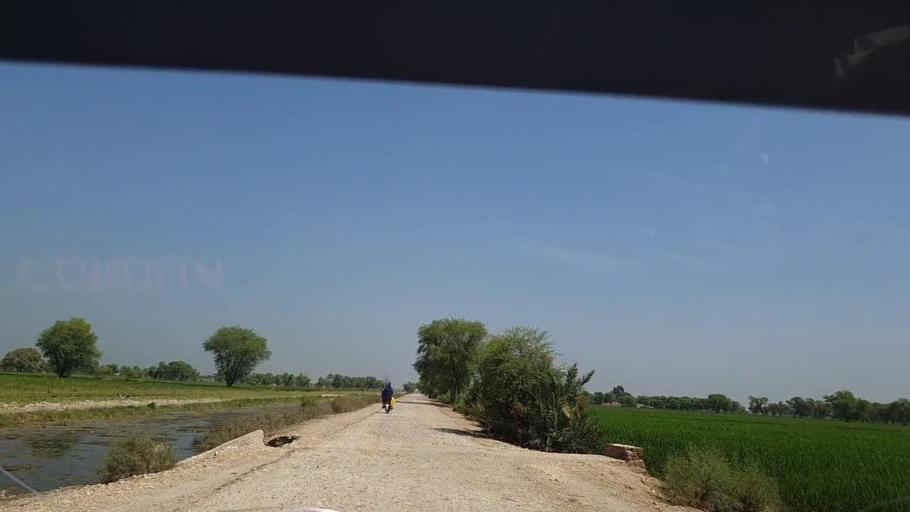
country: PK
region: Sindh
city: Tangwani
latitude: 28.2832
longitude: 69.0278
